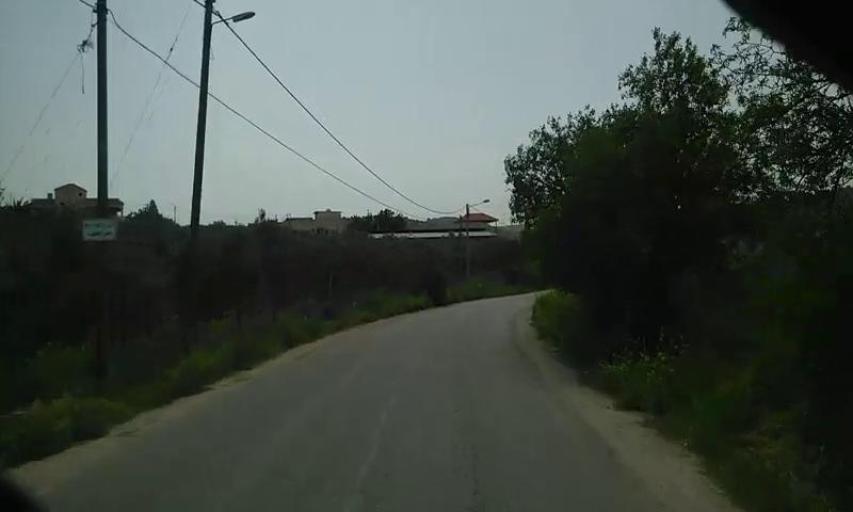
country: PS
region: West Bank
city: Silat al Harithiyah
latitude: 32.5172
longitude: 35.2177
